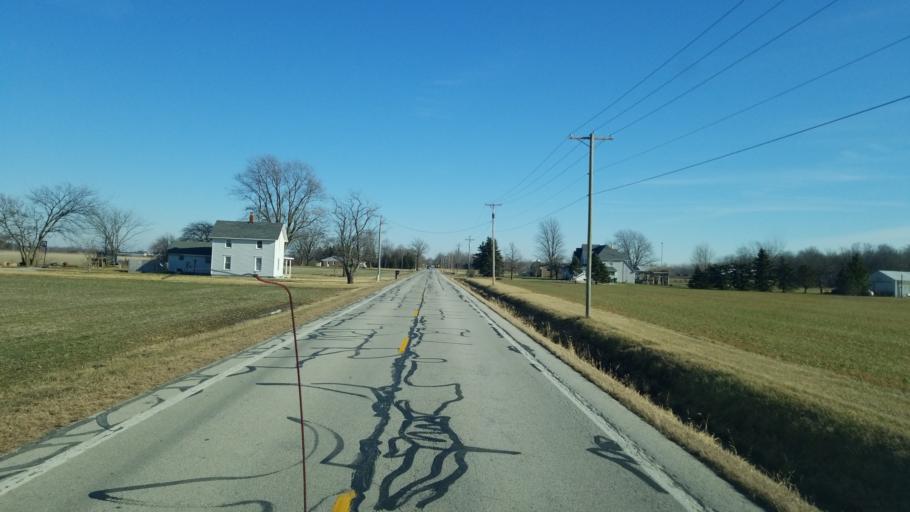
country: US
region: Ohio
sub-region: Wood County
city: Luckey
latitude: 41.4570
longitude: -83.5006
